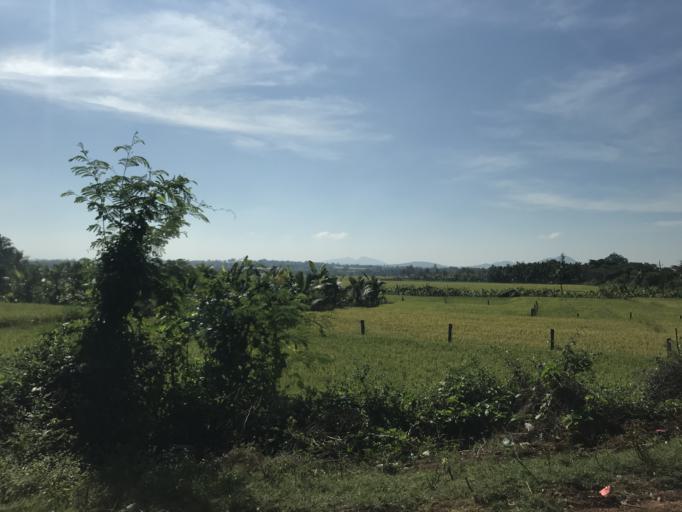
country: IN
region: Karnataka
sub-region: Mysore
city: Heggadadevankote
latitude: 12.1242
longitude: 76.4243
